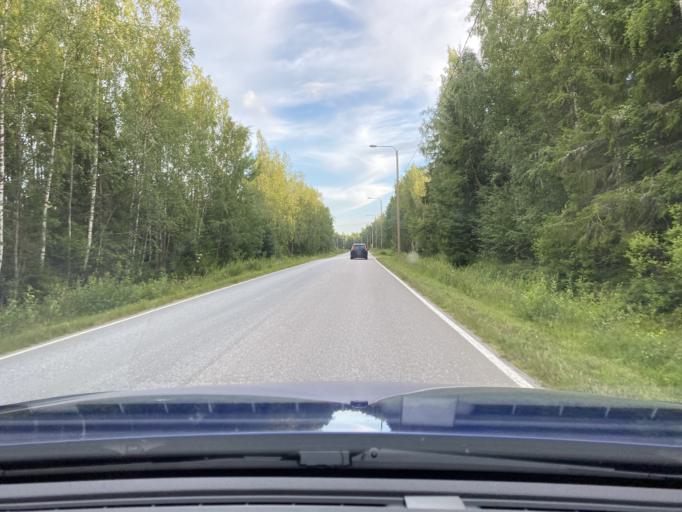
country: FI
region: Ostrobothnia
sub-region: Vaasa
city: Korsnaes
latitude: 62.9487
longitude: 21.1760
